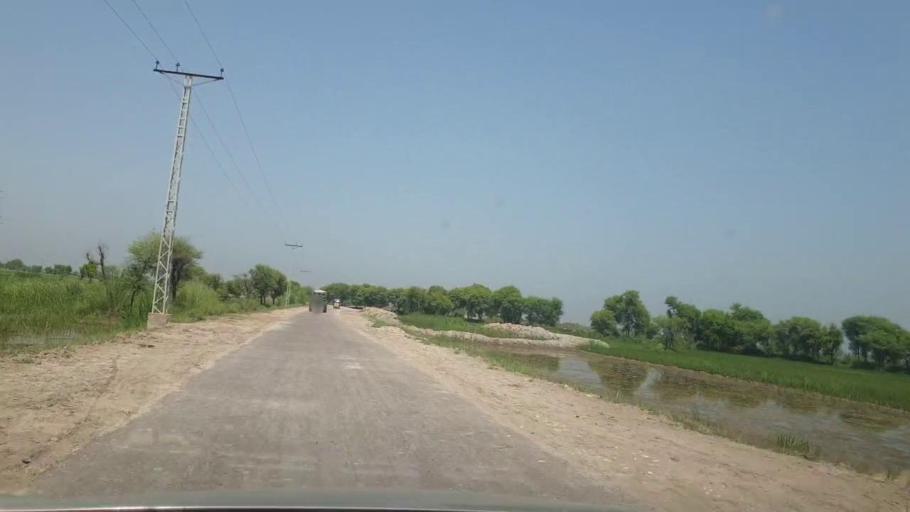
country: PK
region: Sindh
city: Warah
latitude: 27.4695
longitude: 67.7639
